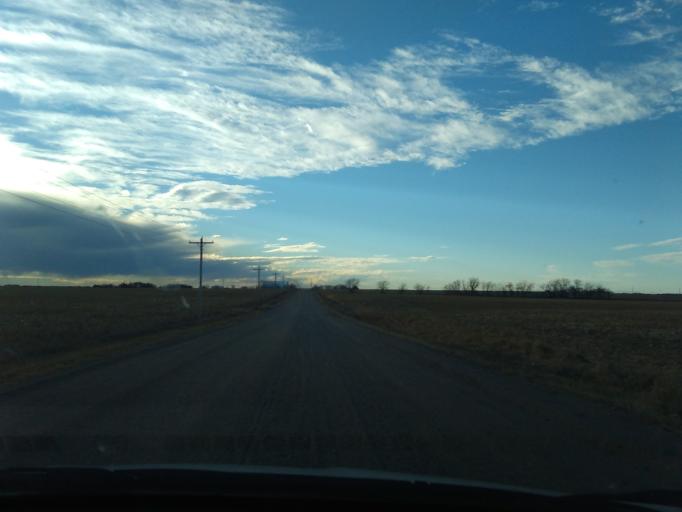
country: US
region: Nebraska
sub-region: Phelps County
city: Holdrege
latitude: 40.4086
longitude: -99.3086
